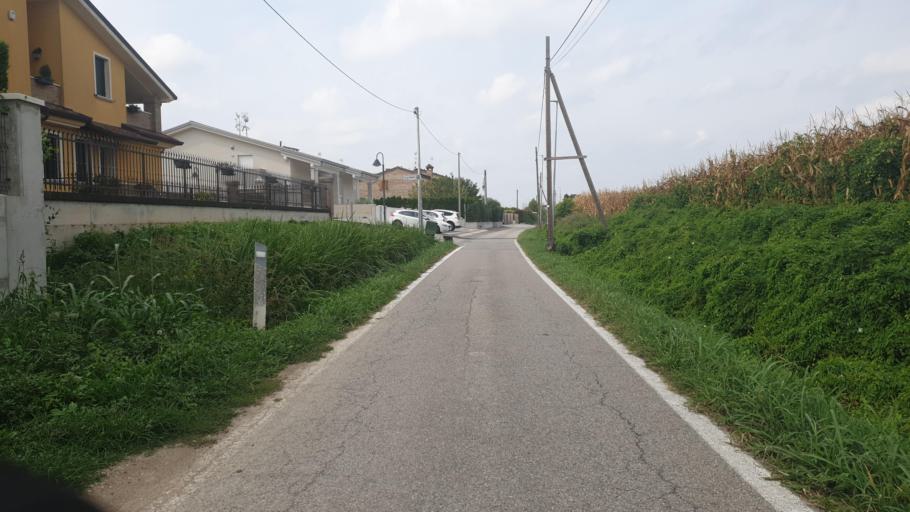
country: IT
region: Veneto
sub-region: Provincia di Padova
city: Albignasego
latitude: 45.3343
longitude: 11.8854
